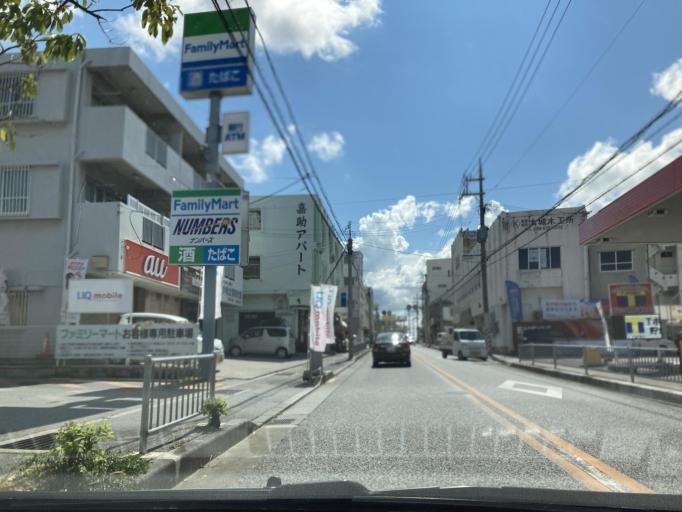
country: JP
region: Okinawa
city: Tomigusuku
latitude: 26.1992
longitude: 127.7012
